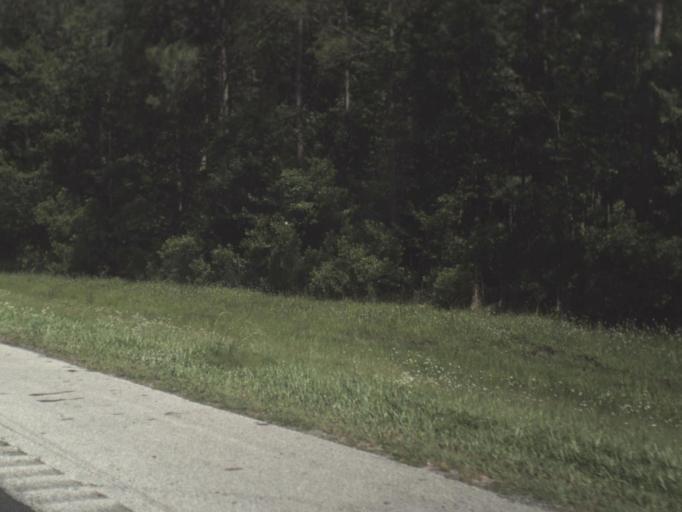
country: US
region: Florida
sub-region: Duval County
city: Baldwin
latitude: 30.2938
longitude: -81.9489
